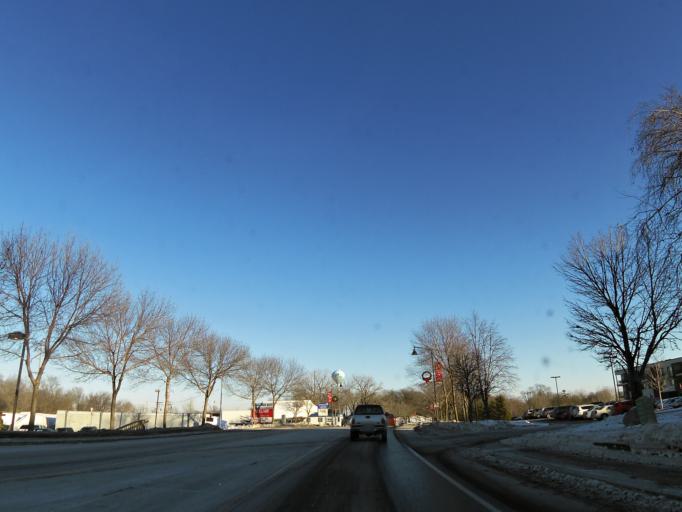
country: US
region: Minnesota
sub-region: Hennepin County
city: Spring Park
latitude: 44.9362
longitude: -93.6390
